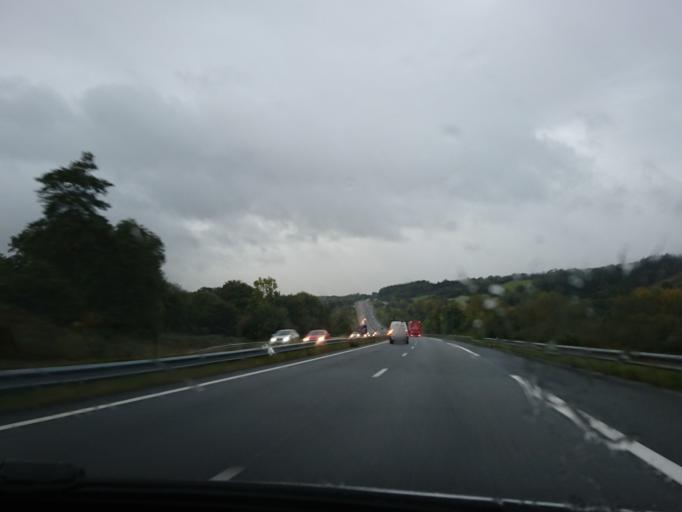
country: FR
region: Brittany
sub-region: Departement du Finistere
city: Hopital-Camfrout
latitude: 48.3159
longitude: -4.2157
